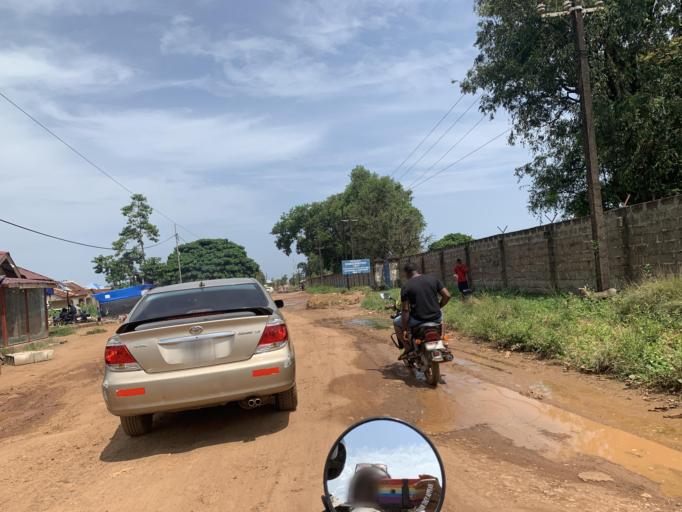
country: SL
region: Western Area
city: Hastings
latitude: 8.4014
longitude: -13.1380
